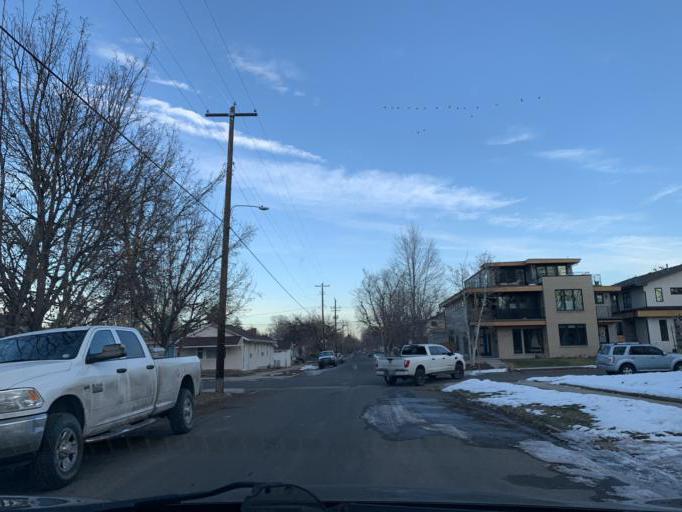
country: US
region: Colorado
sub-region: Adams County
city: Berkley
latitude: 39.7784
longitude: -105.0420
